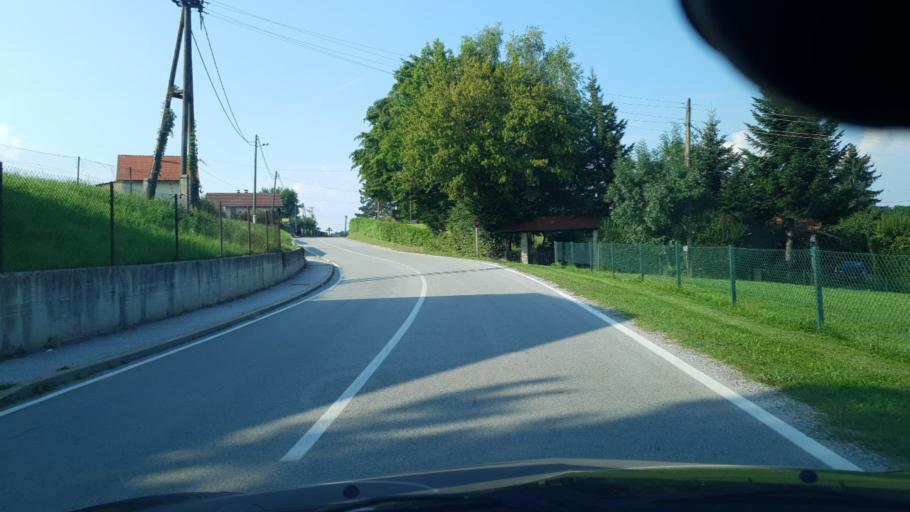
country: HR
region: Krapinsko-Zagorska
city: Oroslavje
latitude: 45.9696
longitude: 15.9160
